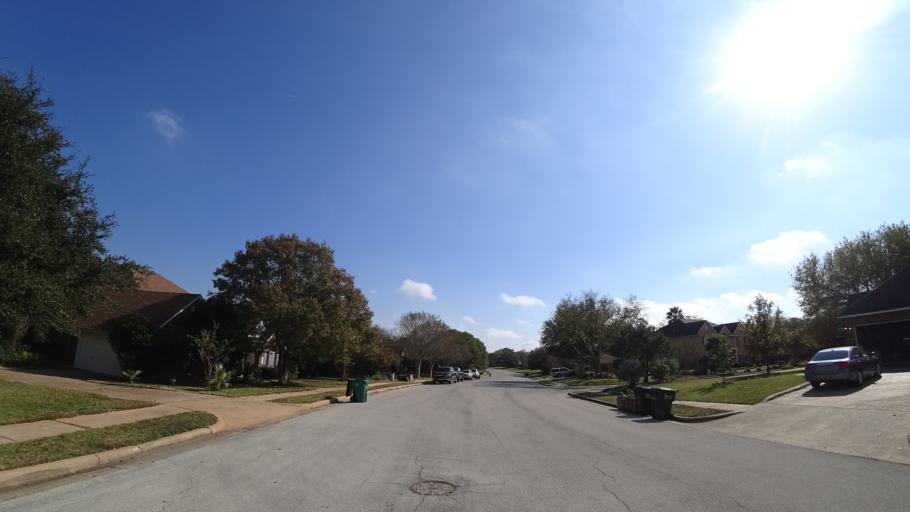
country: US
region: Texas
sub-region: Travis County
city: Shady Hollow
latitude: 30.1683
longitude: -97.8704
